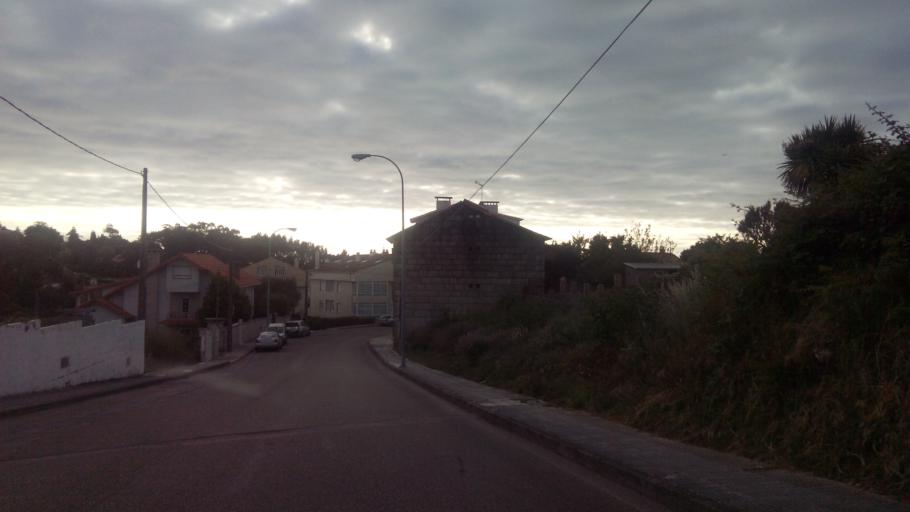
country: ES
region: Galicia
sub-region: Provincia de Pontevedra
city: Nigran
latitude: 42.1231
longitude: -8.8158
